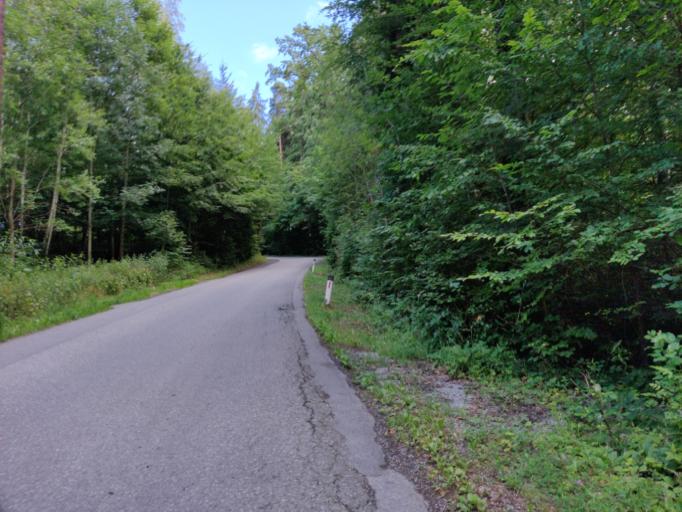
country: AT
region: Styria
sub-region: Politischer Bezirk Graz-Umgebung
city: Thal
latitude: 47.0746
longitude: 15.3388
